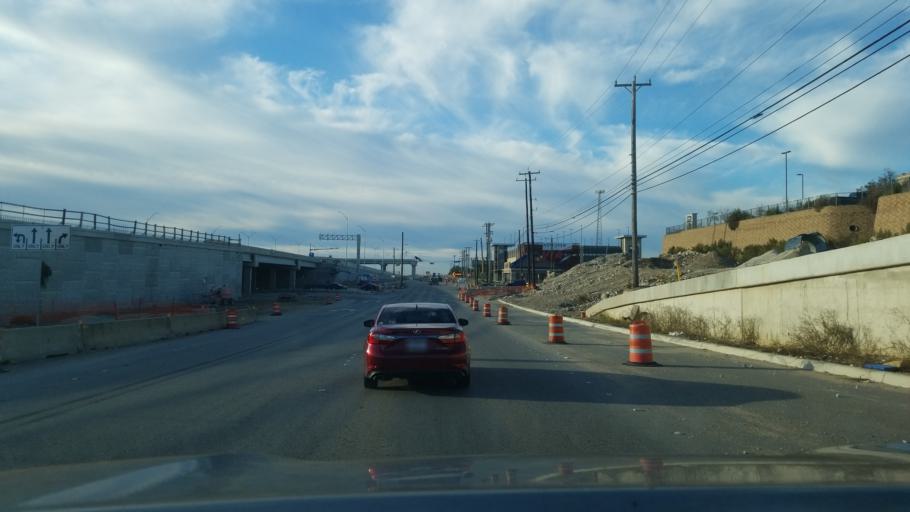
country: US
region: Texas
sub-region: Bexar County
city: Hollywood Park
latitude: 29.6503
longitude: -98.4507
